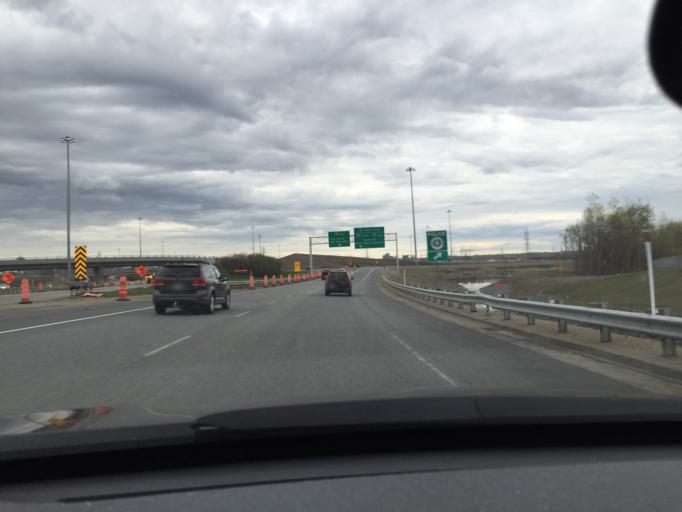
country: CA
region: Quebec
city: Quebec
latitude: 46.8402
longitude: -71.2674
